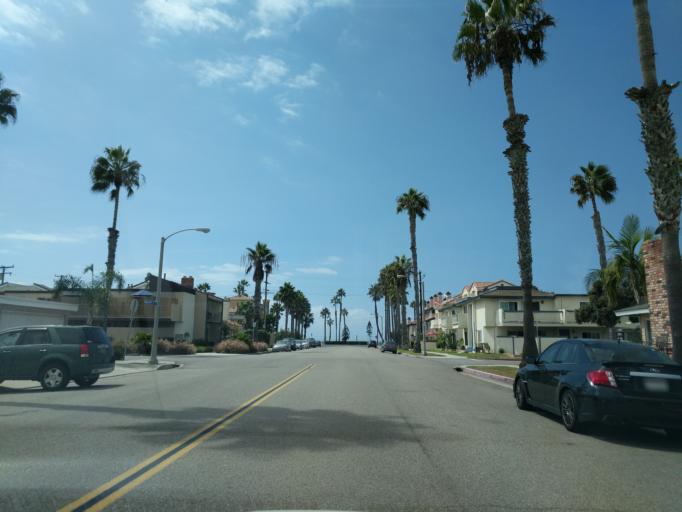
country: US
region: California
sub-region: Orange County
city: Huntington Beach
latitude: 33.6641
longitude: -118.0090
